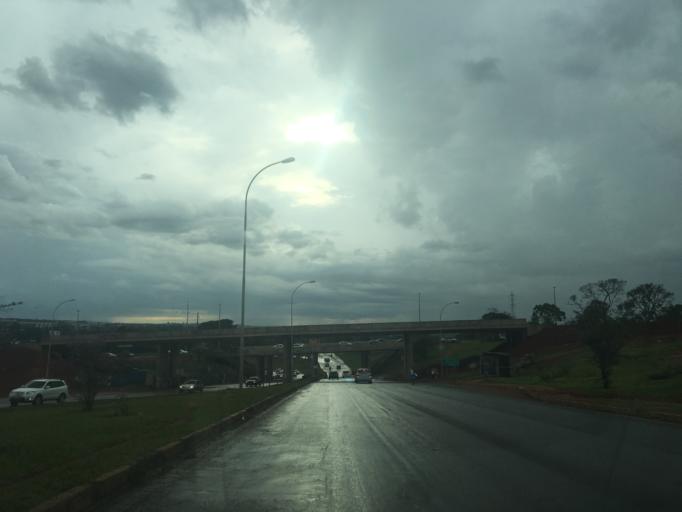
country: BR
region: Federal District
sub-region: Brasilia
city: Brasilia
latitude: -15.7238
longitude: -47.8947
